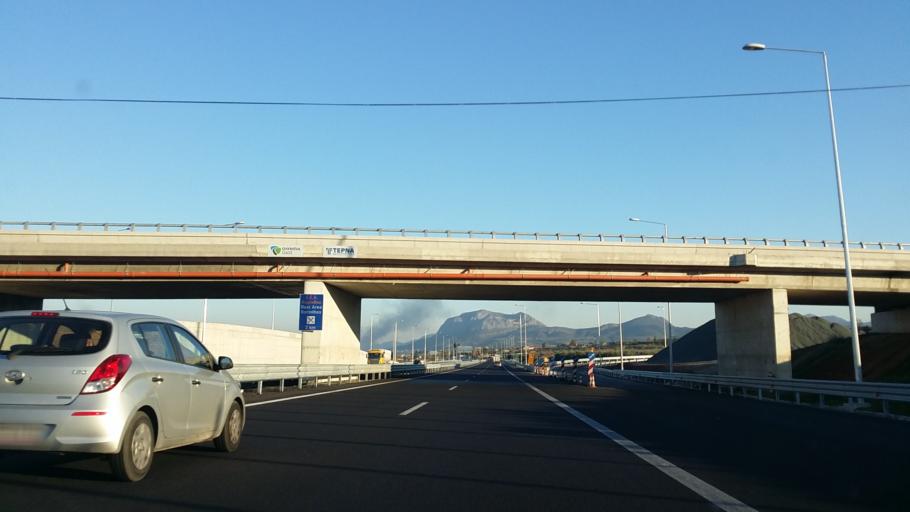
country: GR
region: Peloponnese
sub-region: Nomos Korinthias
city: Zevgolateio
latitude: 37.9292
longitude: 22.7886
